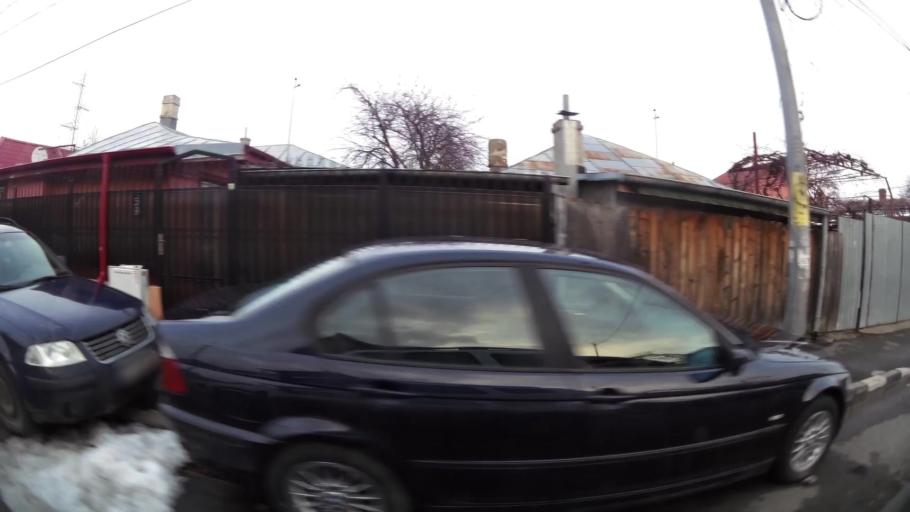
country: RO
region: Ilfov
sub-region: Voluntari City
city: Voluntari
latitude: 44.4758
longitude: 26.1732
